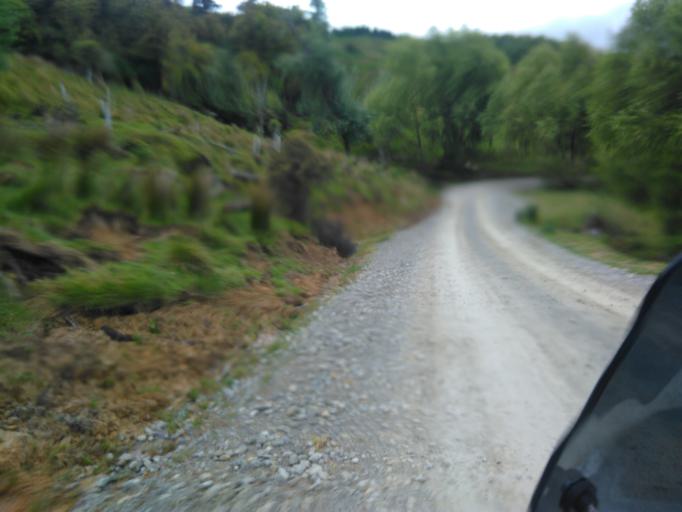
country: NZ
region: Gisborne
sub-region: Gisborne District
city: Gisborne
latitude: -38.0958
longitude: 178.0952
